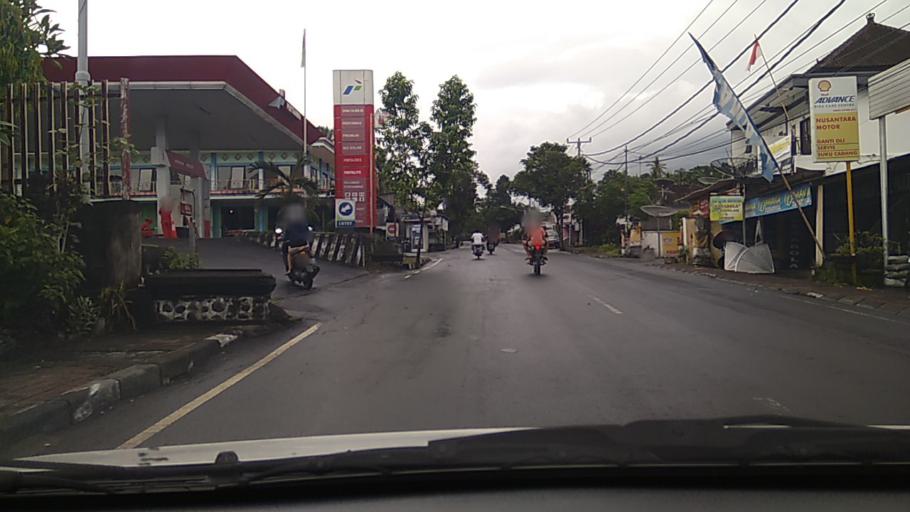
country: ID
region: Bali
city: Subagan
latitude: -8.4375
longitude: 115.5932
